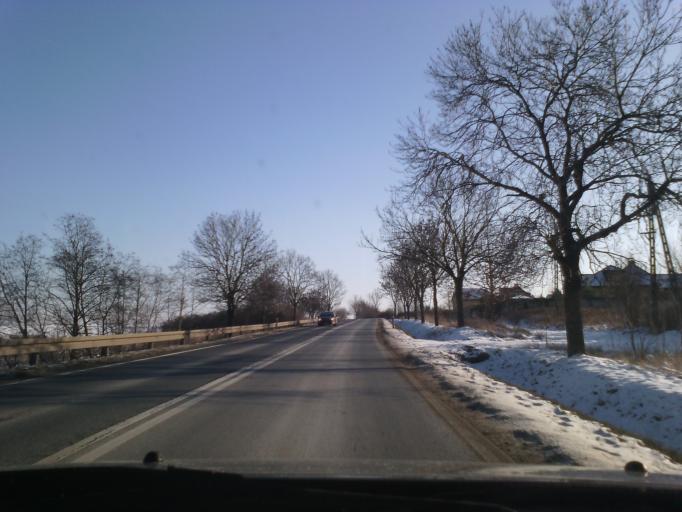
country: PL
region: Lower Silesian Voivodeship
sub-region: Powiat swidnicki
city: Strzegom
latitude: 50.9522
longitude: 16.3570
